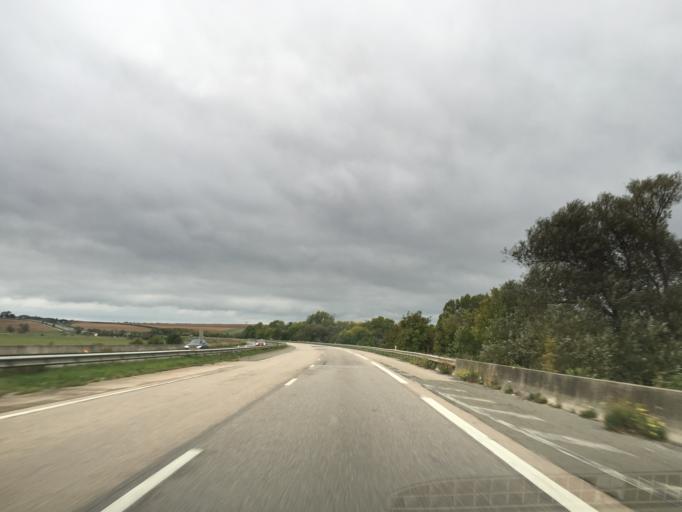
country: FR
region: Lorraine
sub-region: Departement de Meurthe-et-Moselle
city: Foug
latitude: 48.6879
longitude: 5.7074
